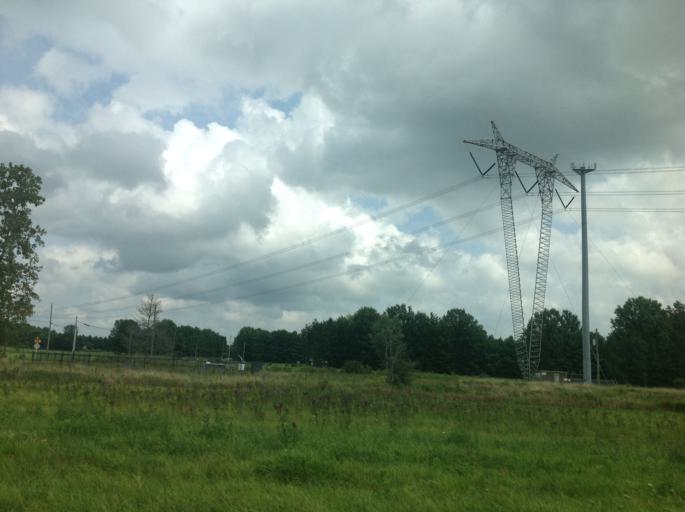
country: US
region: Ohio
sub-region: Delaware County
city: Sunbury
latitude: 40.2164
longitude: -82.9130
